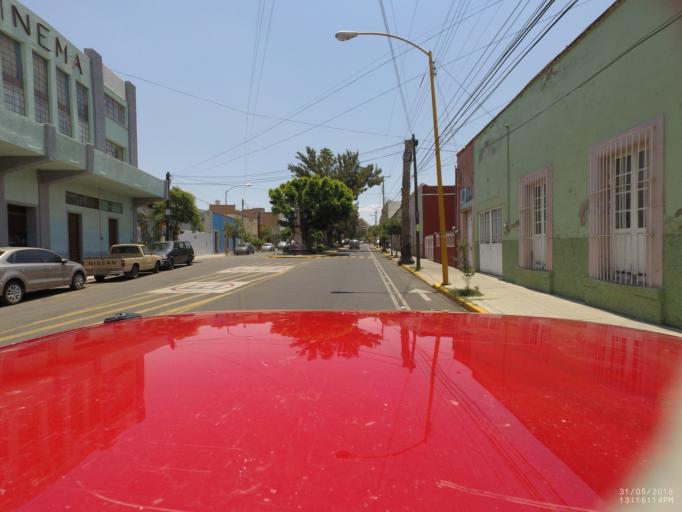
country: MX
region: Aguascalientes
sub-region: Aguascalientes
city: Aguascalientes
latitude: 21.8822
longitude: -102.2878
